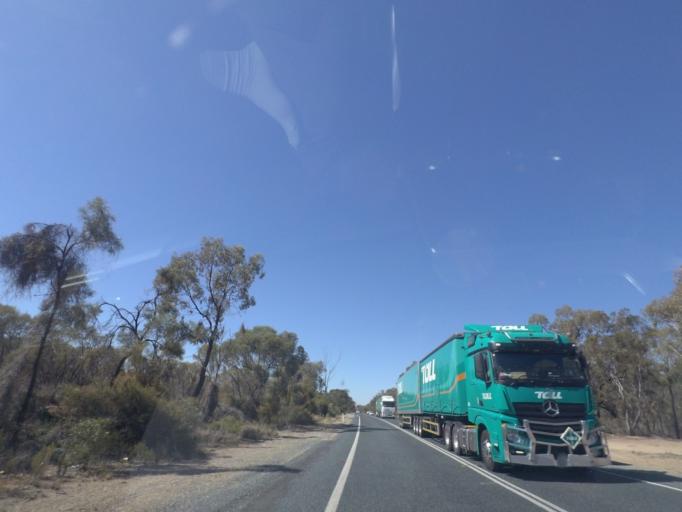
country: AU
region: New South Wales
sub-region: Bland
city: West Wyalong
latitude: -34.1397
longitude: 147.1204
